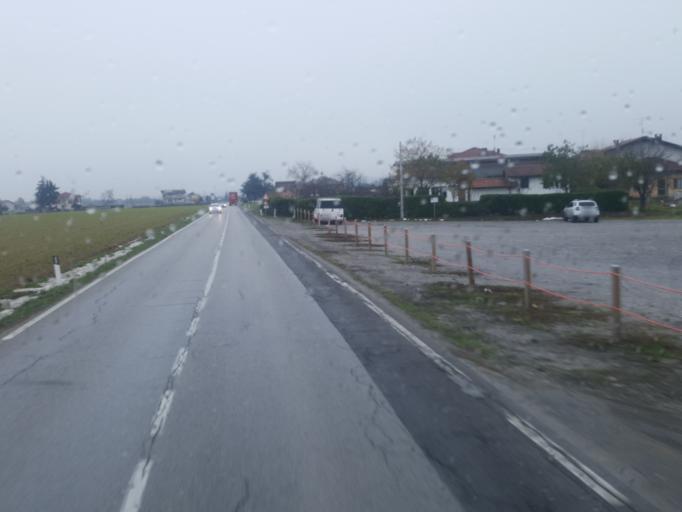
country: IT
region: Piedmont
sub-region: Provincia di Cuneo
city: Breo
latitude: 44.4064
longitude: 7.8345
